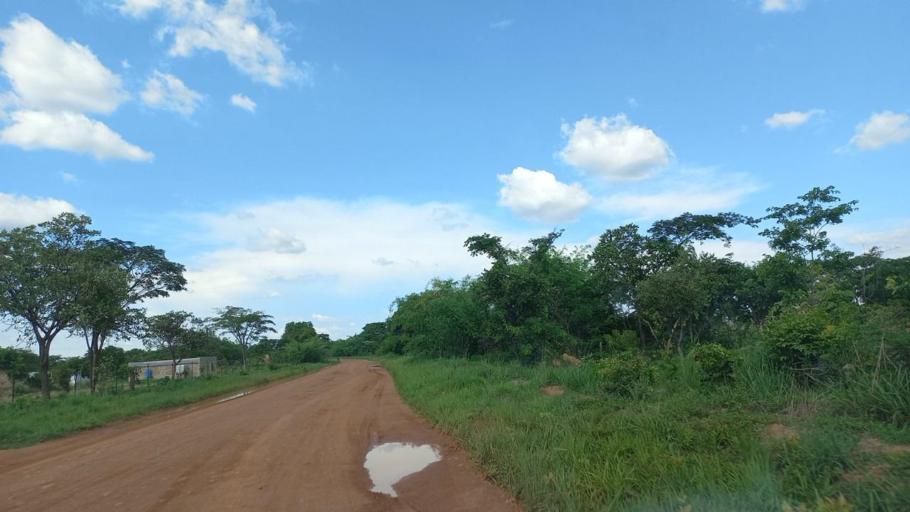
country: ZM
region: Copperbelt
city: Kitwe
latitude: -12.8539
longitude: 28.3888
